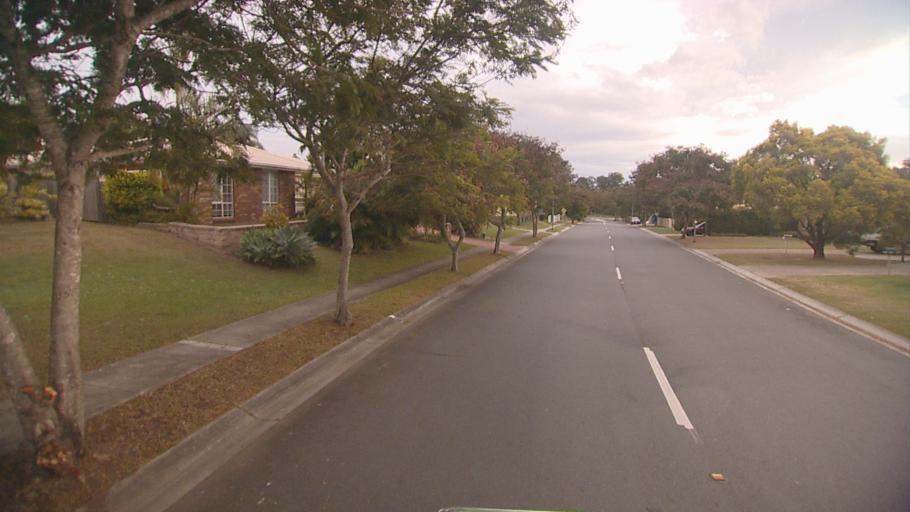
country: AU
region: Queensland
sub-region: Logan
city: Park Ridge South
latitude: -27.6746
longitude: 153.0228
